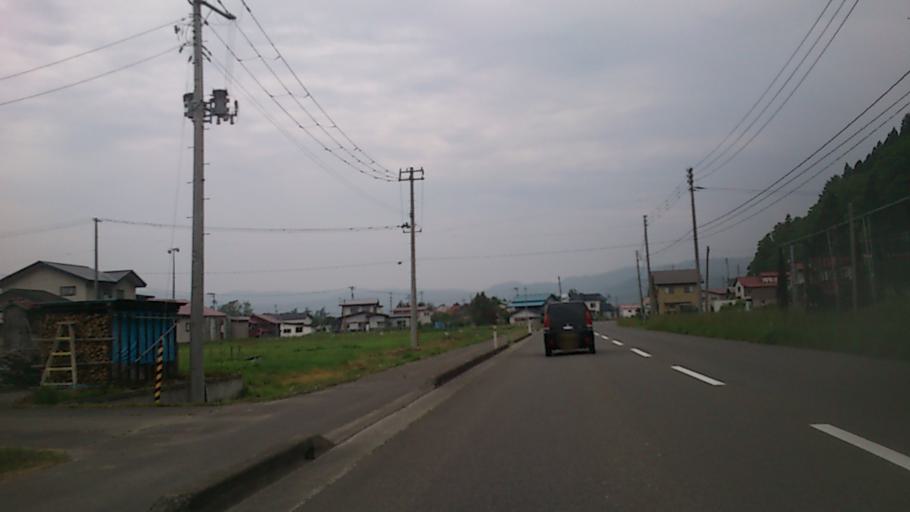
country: JP
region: Aomori
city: Hirosaki
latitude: 40.5906
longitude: 140.3355
